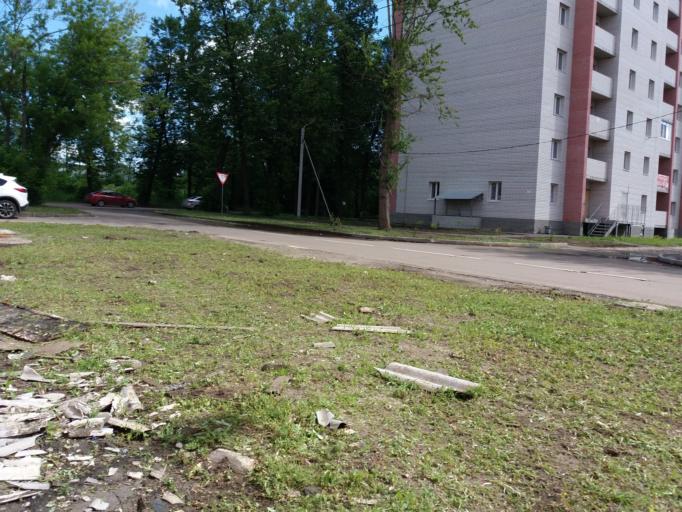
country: RU
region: Jaroslavl
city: Yaroslavl
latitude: 57.6420
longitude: 39.8439
